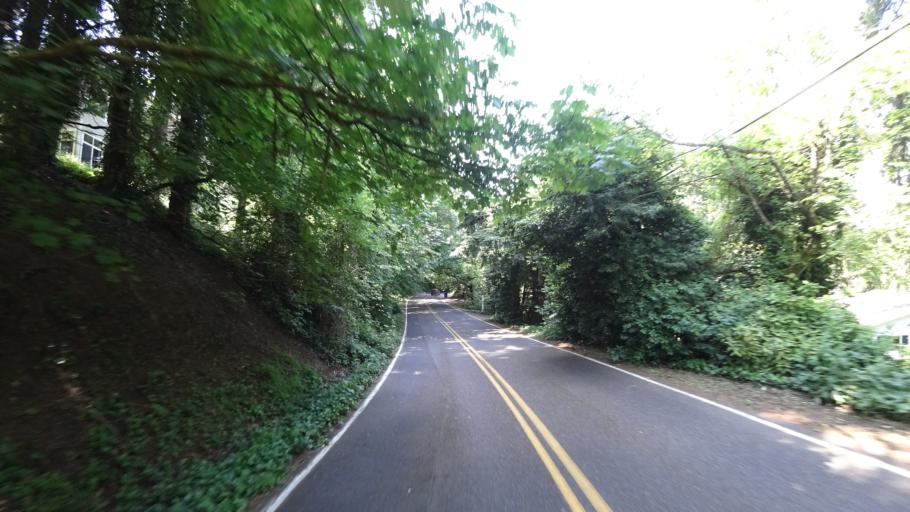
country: US
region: Oregon
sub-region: Clackamas County
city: Lake Oswego
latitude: 45.4415
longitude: -122.6943
